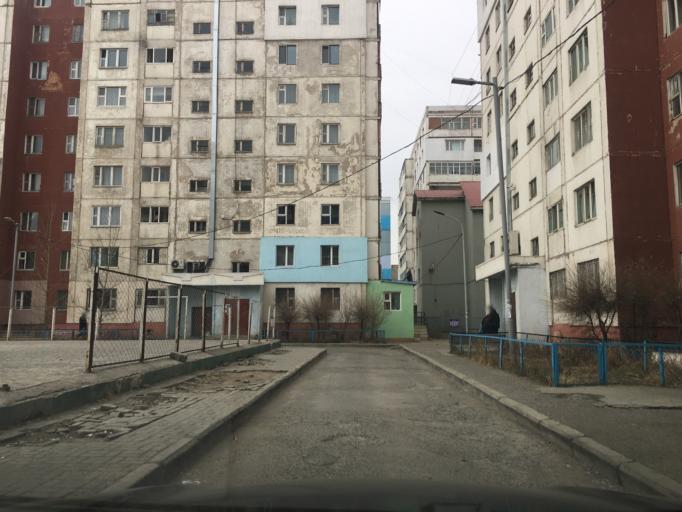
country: MN
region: Ulaanbaatar
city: Ulaanbaatar
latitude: 47.9104
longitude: 106.8901
